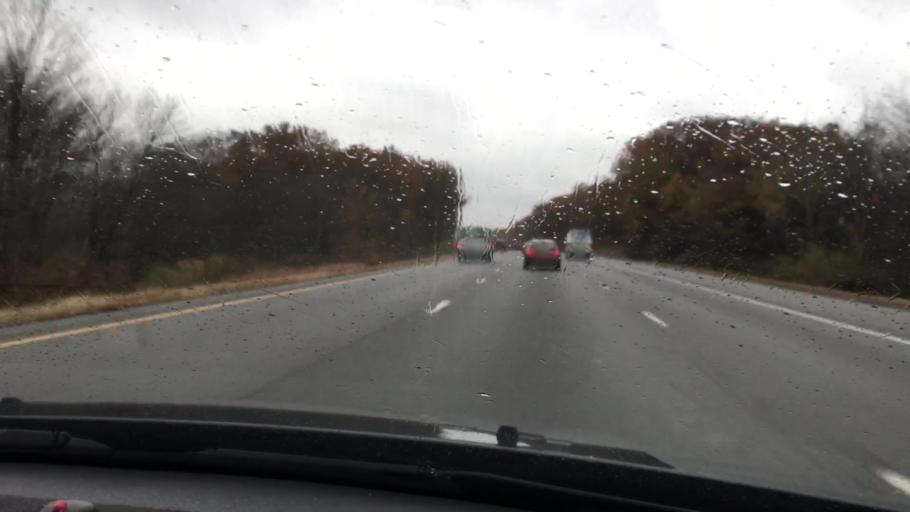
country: US
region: Massachusetts
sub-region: Middlesex County
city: Marlborough
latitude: 42.3296
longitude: -71.5751
